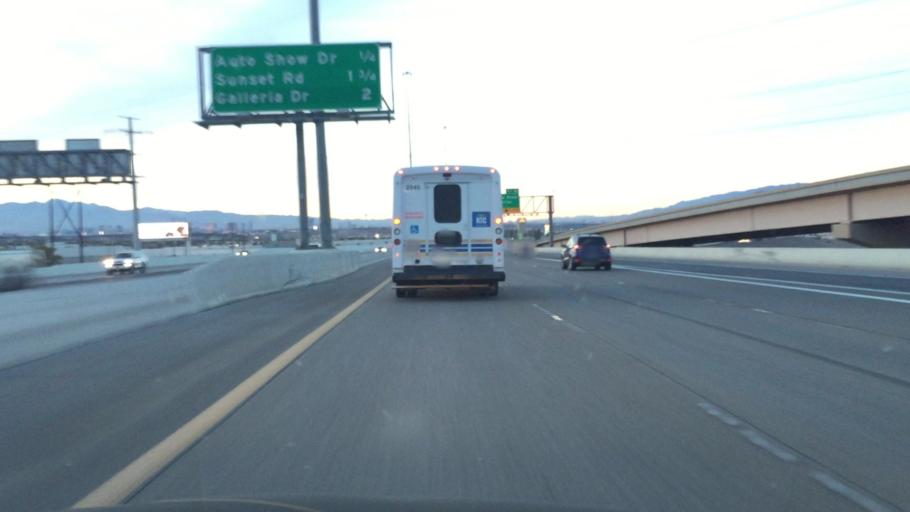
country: US
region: Nevada
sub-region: Clark County
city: Henderson
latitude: 36.0369
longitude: -115.0178
